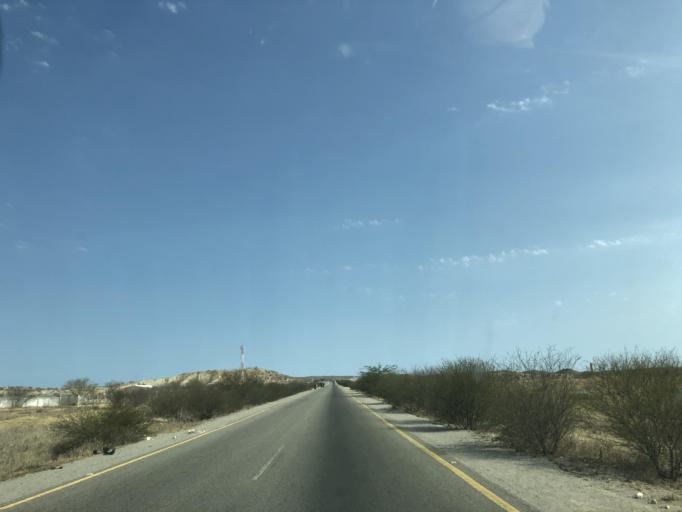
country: AO
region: Benguela
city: Benguela
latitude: -12.7400
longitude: 13.3514
